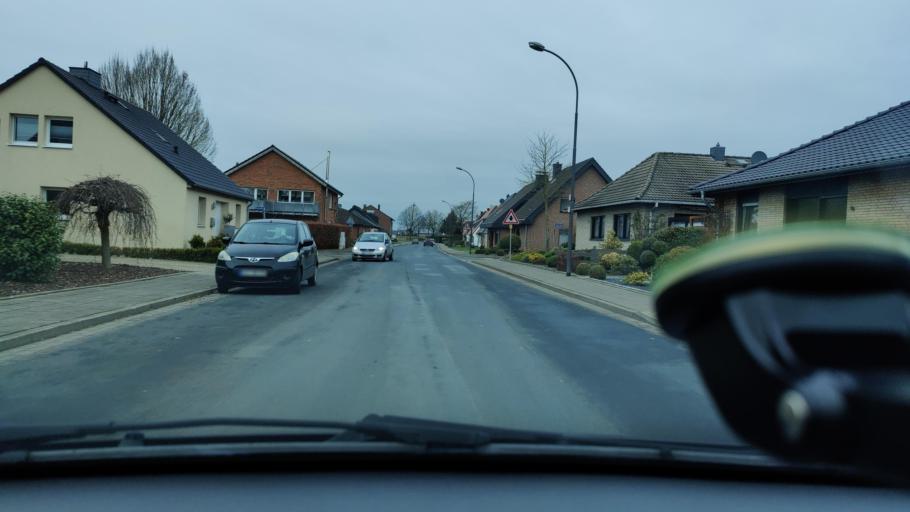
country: DE
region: North Rhine-Westphalia
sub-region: Regierungsbezirk Dusseldorf
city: Uedem
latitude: 51.6711
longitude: 6.2728
